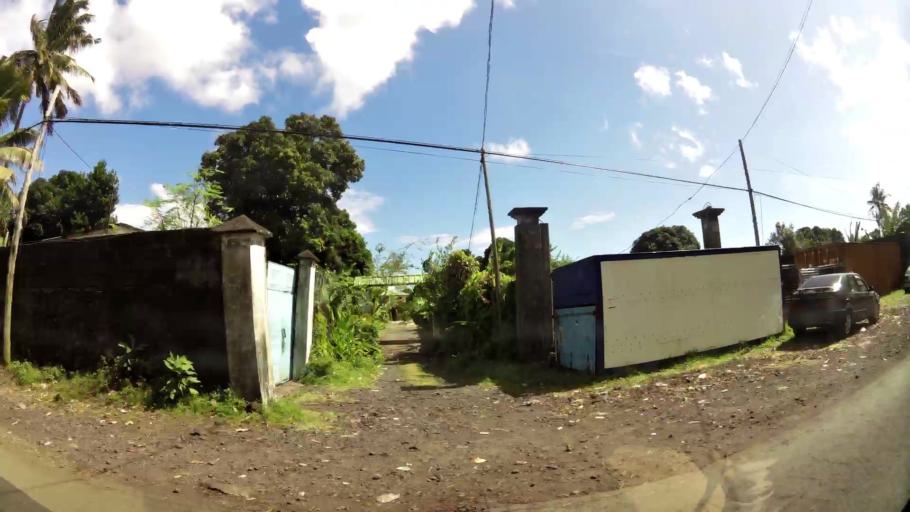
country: KM
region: Grande Comore
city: Mavingouni
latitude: -11.7275
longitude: 43.2495
